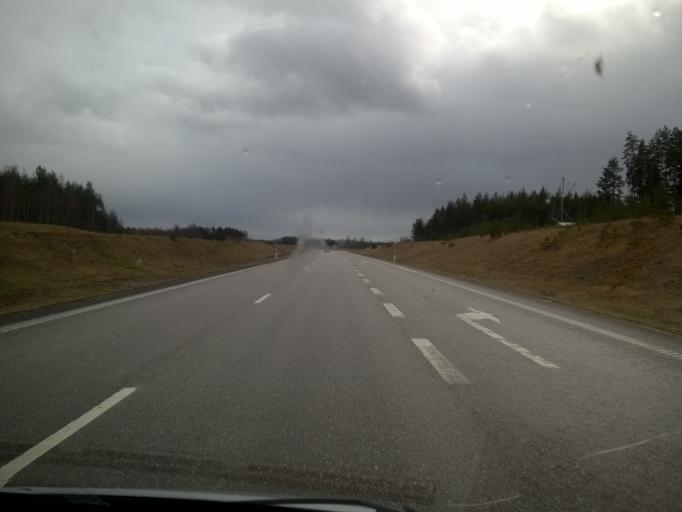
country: SE
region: Uppsala
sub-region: Osthammars Kommun
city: Bjorklinge
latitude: 60.0167
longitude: 17.6235
